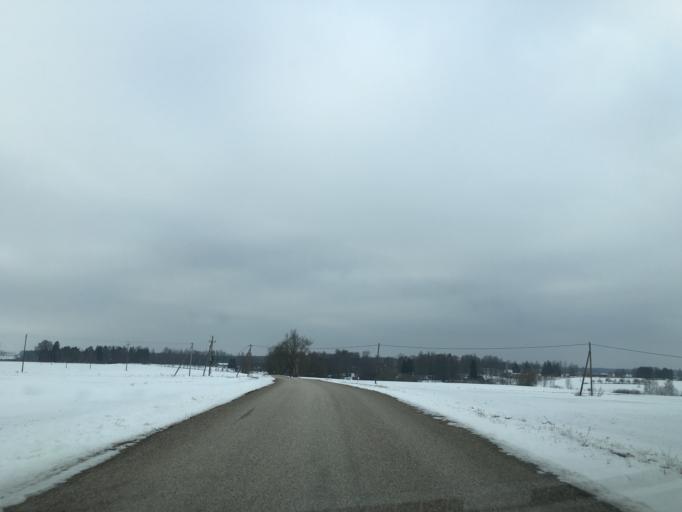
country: EE
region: Tartu
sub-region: Elva linn
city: Elva
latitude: 58.1026
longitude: 26.2126
